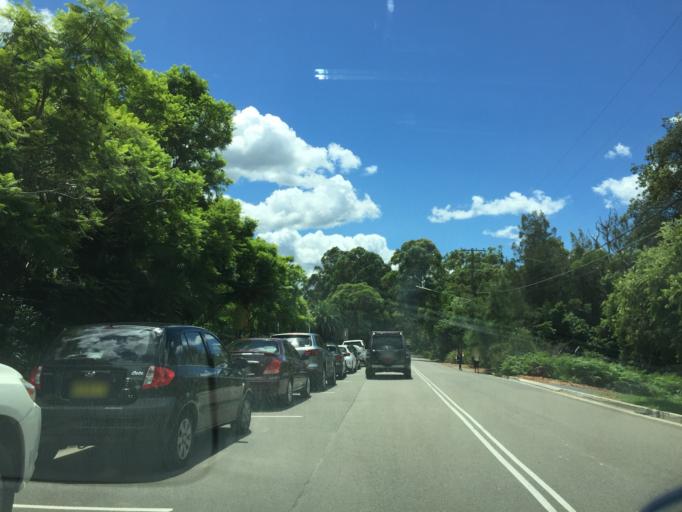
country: AU
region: New South Wales
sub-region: Ryde
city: North Ryde
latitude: -33.7944
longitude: 151.1415
